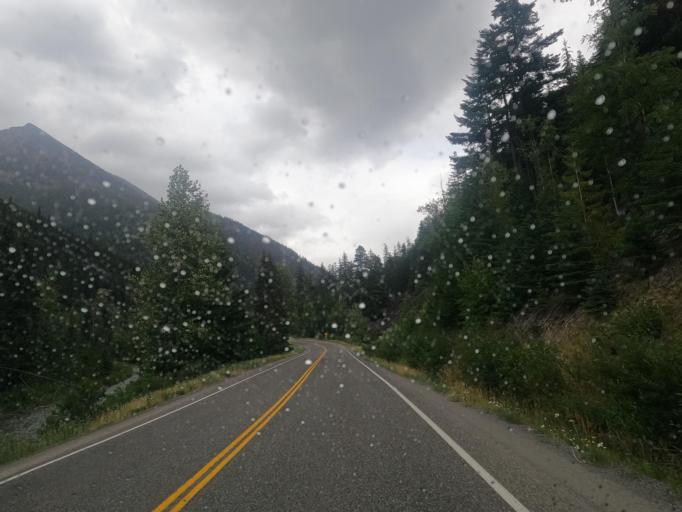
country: CA
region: British Columbia
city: Lillooet
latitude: 50.4851
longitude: -122.2070
